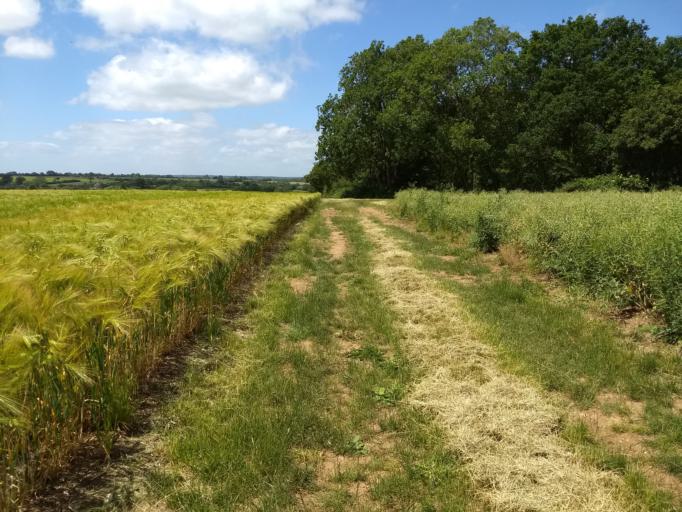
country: GB
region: England
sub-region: Milton Keynes
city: Calverton
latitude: 52.0192
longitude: -0.8574
